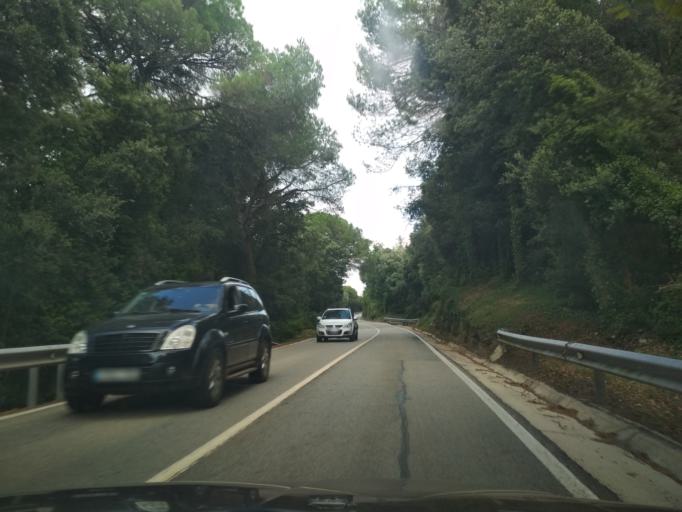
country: ES
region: Catalonia
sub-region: Provincia de Barcelona
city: Sant Feliu de Codines
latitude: 41.7051
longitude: 2.1609
